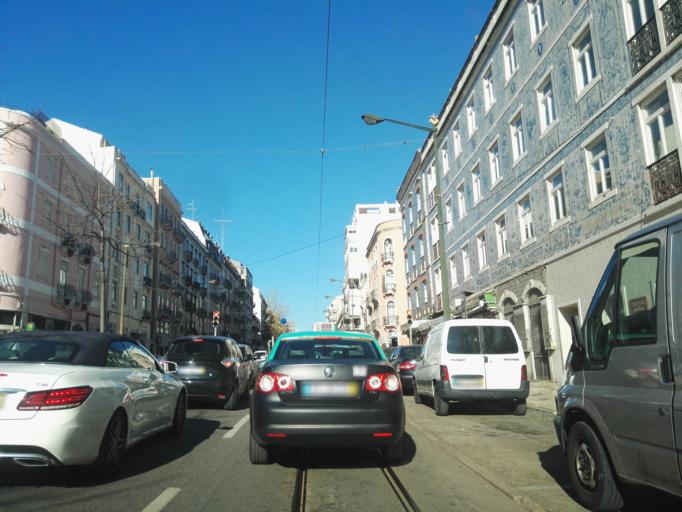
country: PT
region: Lisbon
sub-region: Lisbon
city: Lisbon
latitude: 38.7208
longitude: -9.1354
